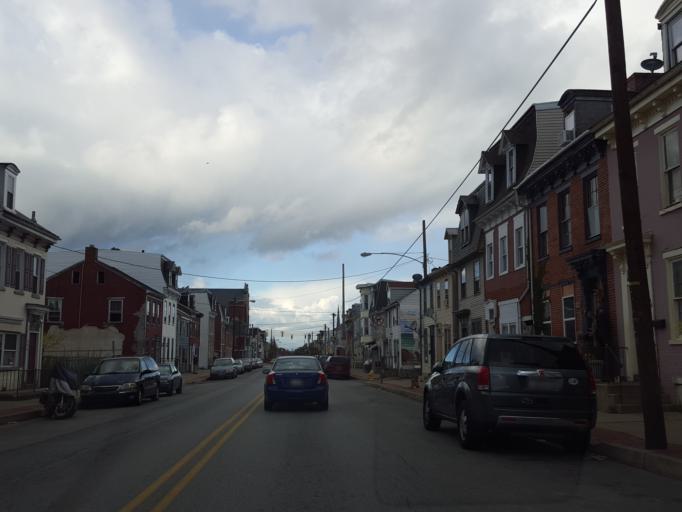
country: US
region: Pennsylvania
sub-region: York County
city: York
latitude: 39.9584
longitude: -76.7212
